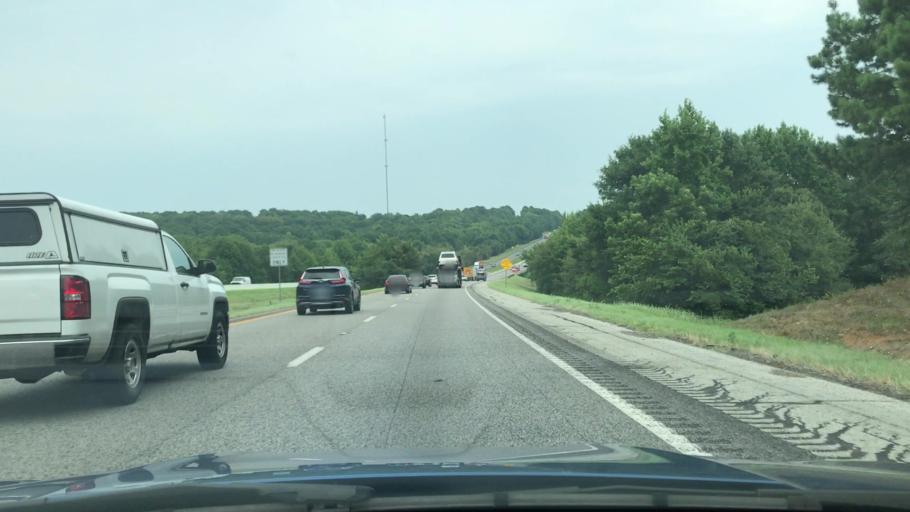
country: US
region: Texas
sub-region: Smith County
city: Lindale
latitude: 32.4682
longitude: -95.3450
